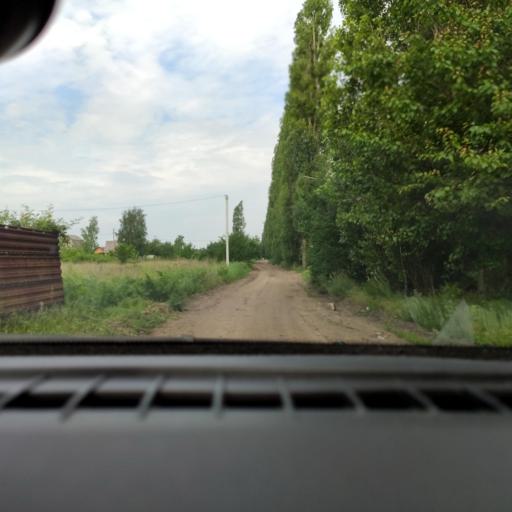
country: RU
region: Voronezj
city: Maslovka
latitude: 51.5014
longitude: 39.1967
